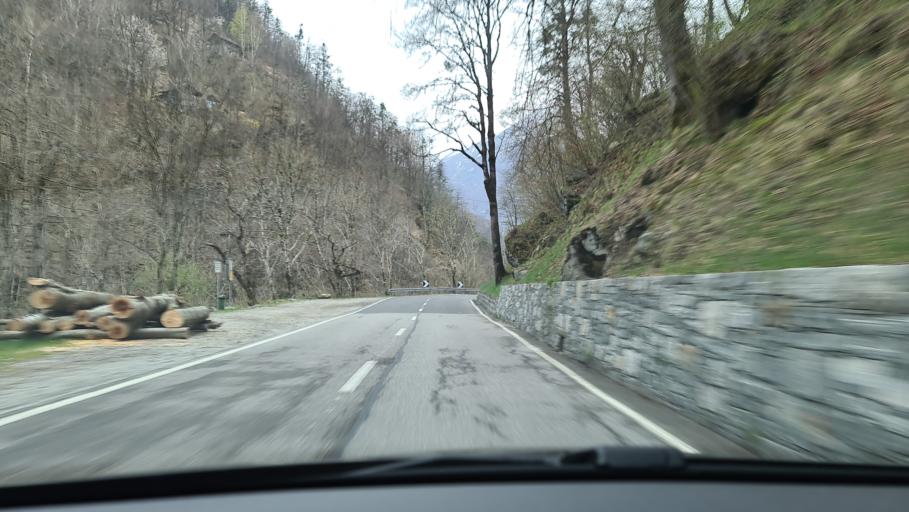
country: CH
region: Ticino
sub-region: Vallemaggia District
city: Cevio
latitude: 46.3593
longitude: 8.6441
